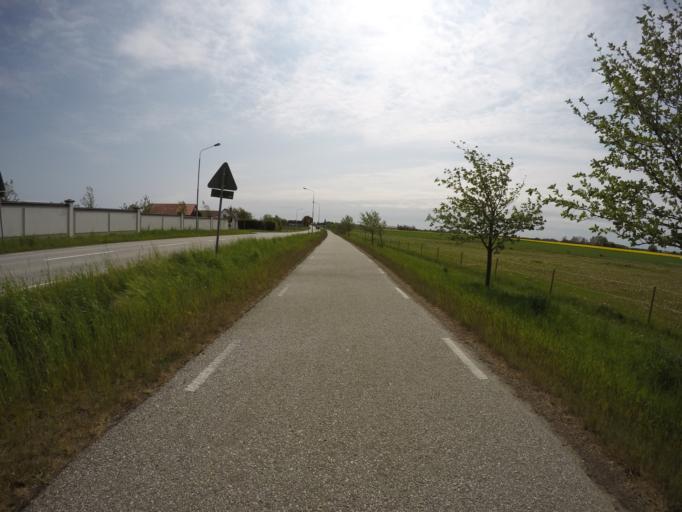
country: SE
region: Skane
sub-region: Malmo
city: Tygelsjo
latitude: 55.5127
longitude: 12.9959
